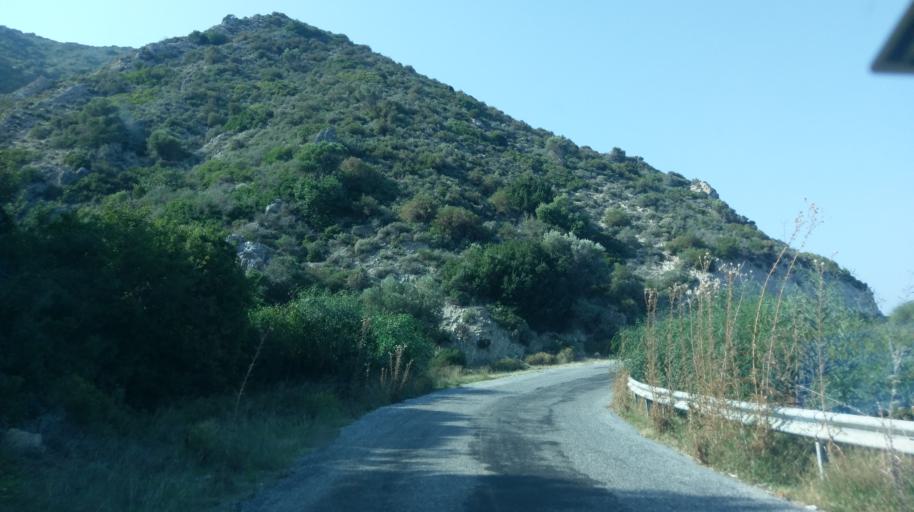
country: CY
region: Keryneia
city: Lapithos
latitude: 35.3657
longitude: 33.0139
